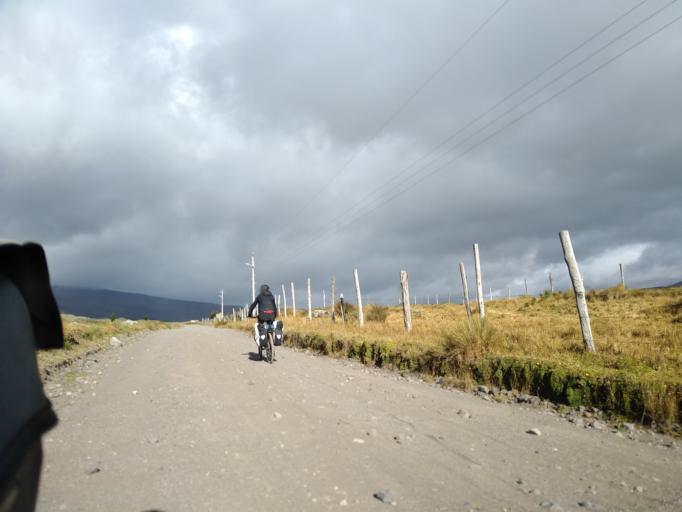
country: EC
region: Pichincha
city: Machachi
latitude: -0.5602
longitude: -78.4496
